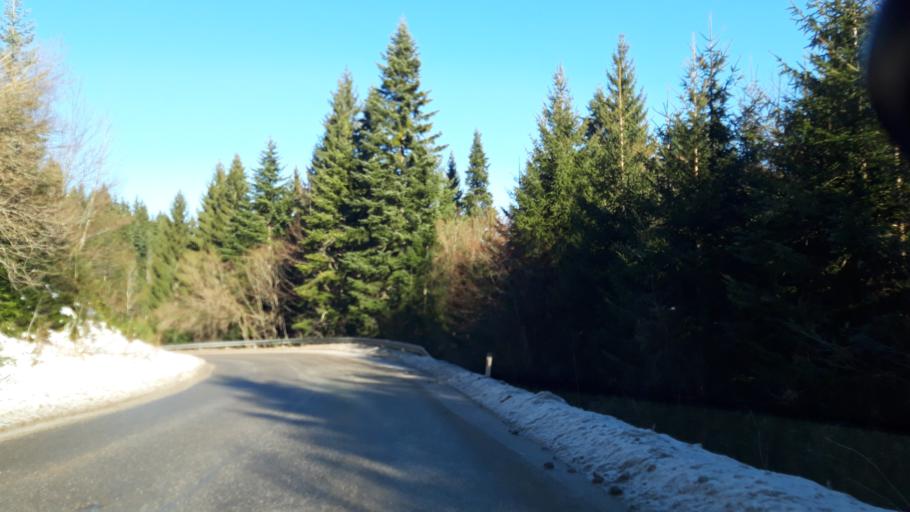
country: BA
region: Republika Srpska
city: Koran
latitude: 43.7985
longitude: 18.5515
